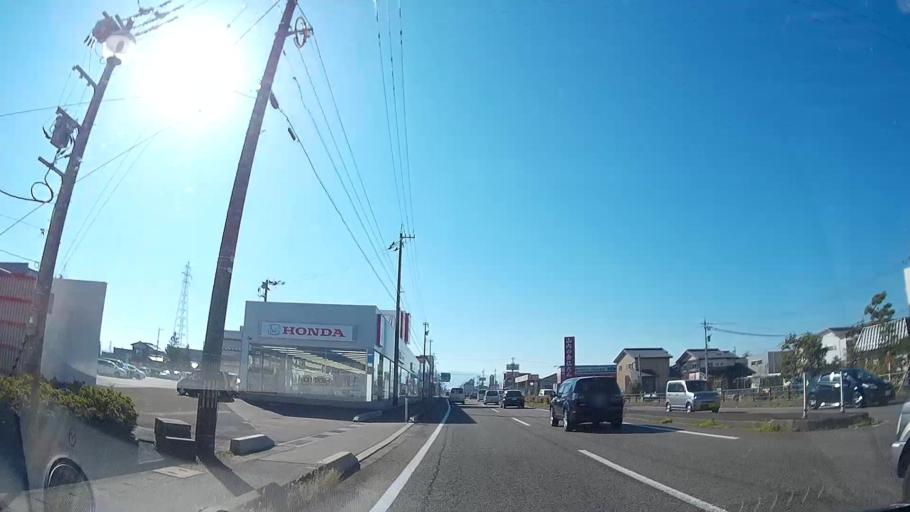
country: JP
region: Toyama
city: Takaoka
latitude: 36.6889
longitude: 136.9769
